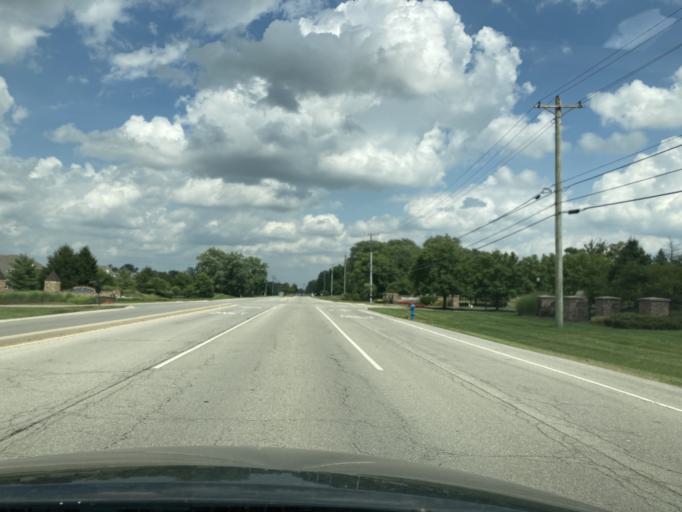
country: US
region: Indiana
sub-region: Boone County
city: Zionsville
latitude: 39.9985
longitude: -86.2569
